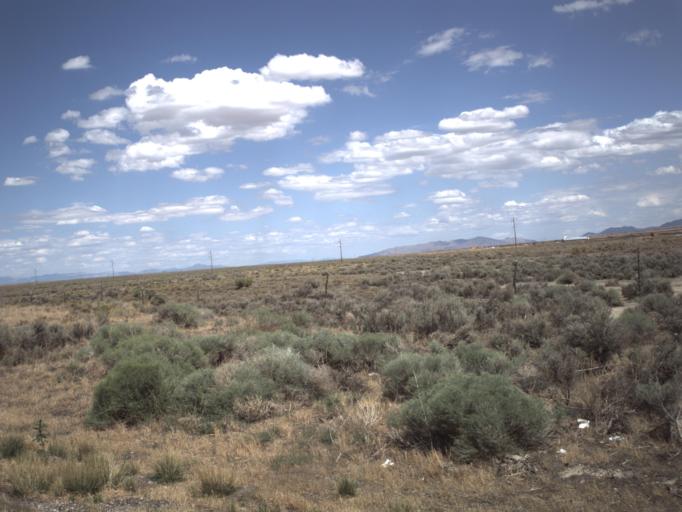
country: US
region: Utah
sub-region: Millard County
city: Delta
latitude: 39.2666
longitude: -112.4516
